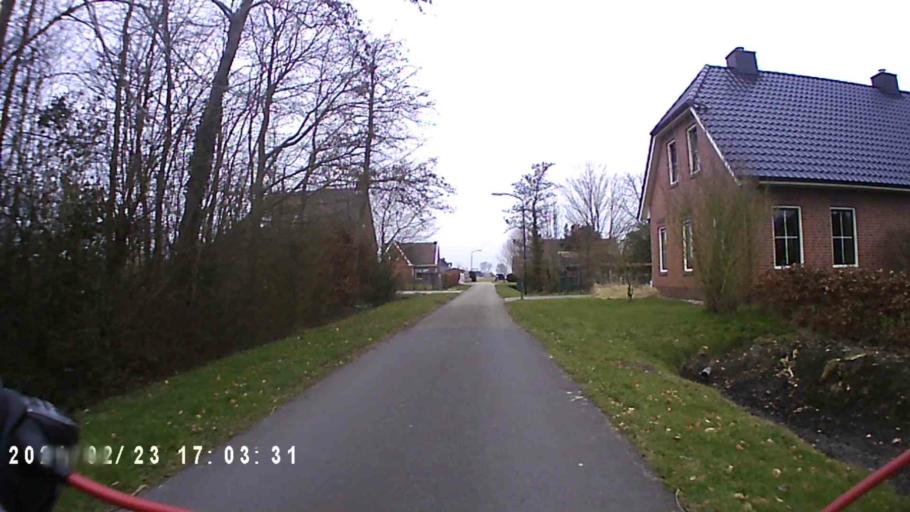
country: NL
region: Groningen
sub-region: Gemeente De Marne
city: Ulrum
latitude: 53.3865
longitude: 6.3840
